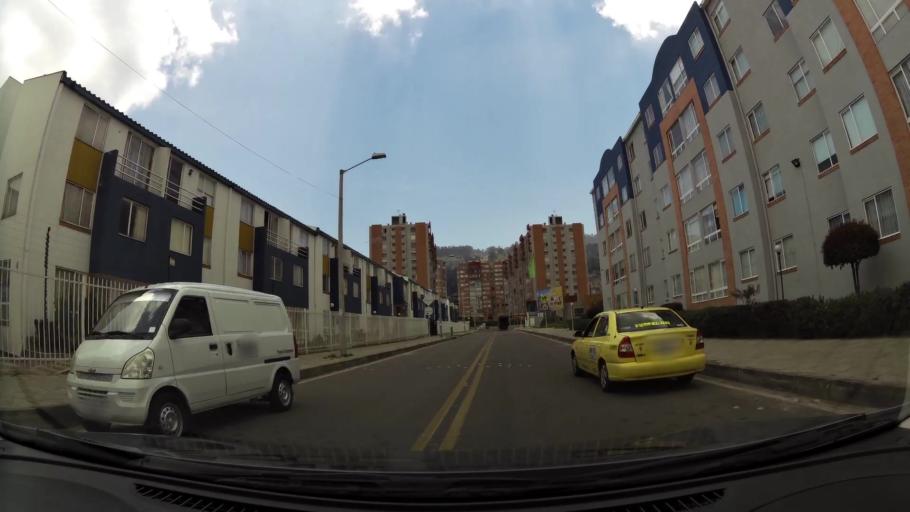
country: CO
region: Cundinamarca
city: La Calera
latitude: 4.7457
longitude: -74.0280
